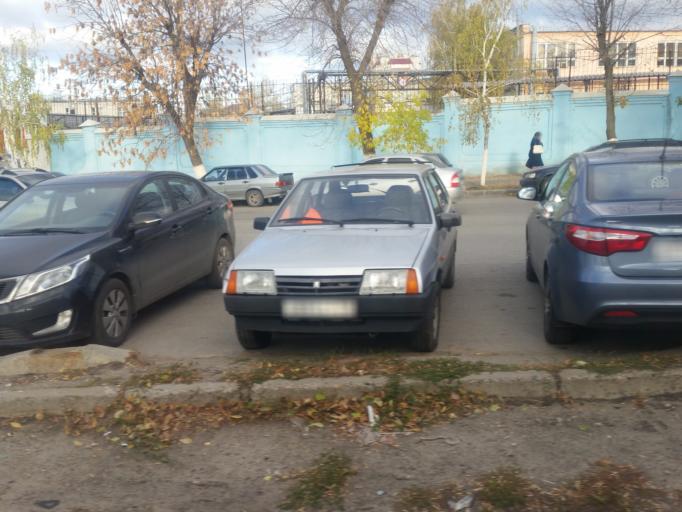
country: RU
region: Ulyanovsk
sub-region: Ulyanovskiy Rayon
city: Ulyanovsk
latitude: 54.3169
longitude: 48.3862
